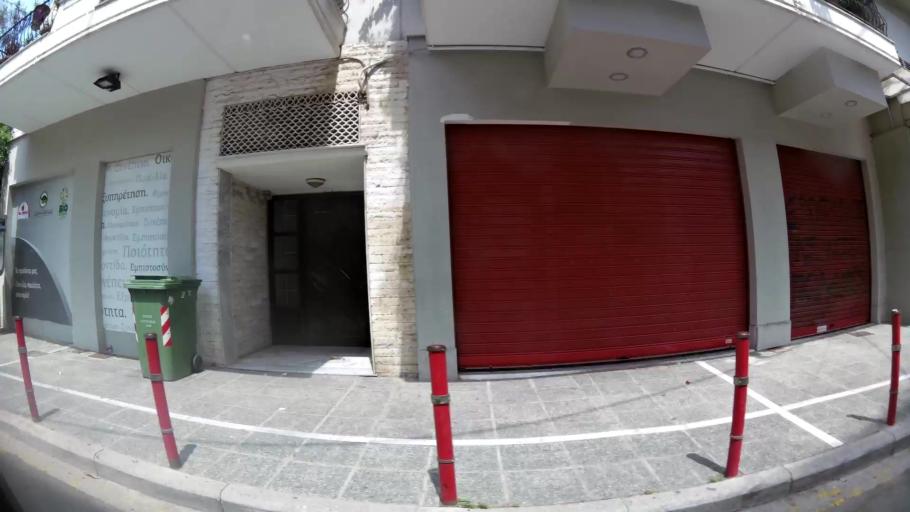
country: GR
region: Central Macedonia
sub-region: Nomos Pierias
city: Katerini
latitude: 40.2700
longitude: 22.5056
